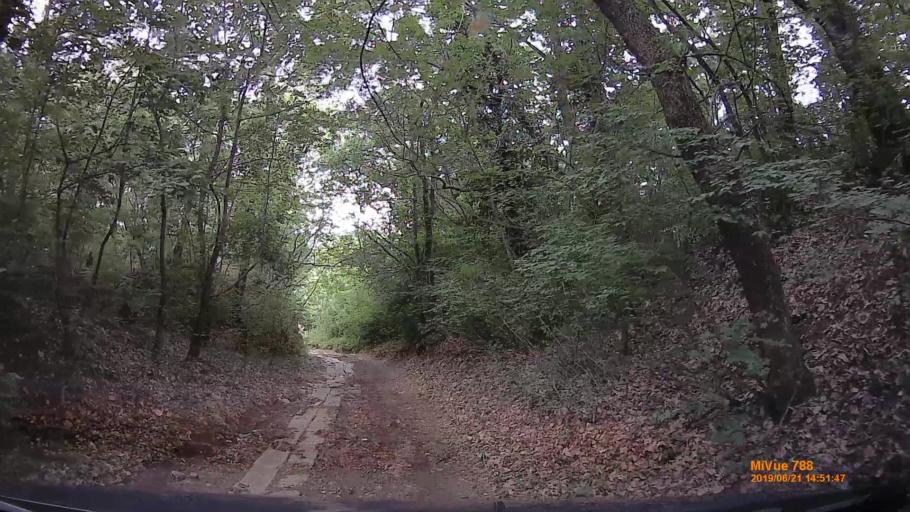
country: HU
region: Baranya
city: Hosszuheteny
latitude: 46.1290
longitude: 18.3103
